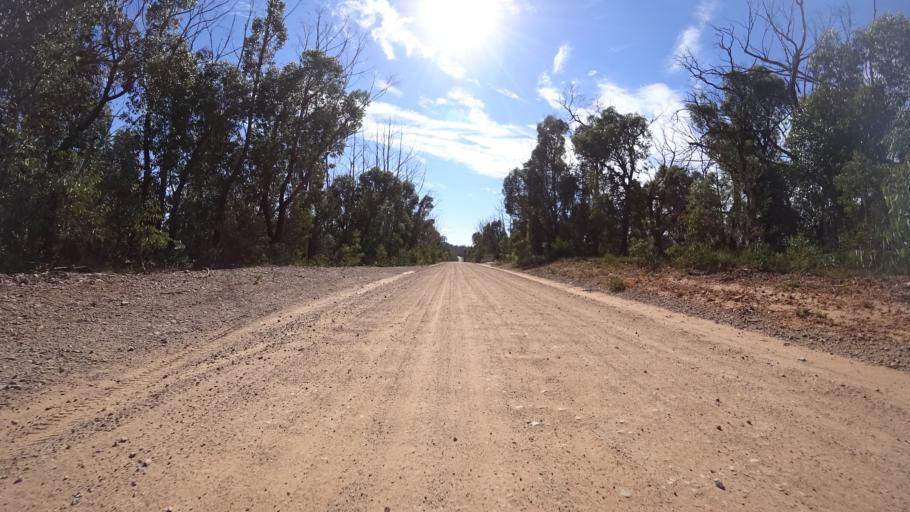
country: AU
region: New South Wales
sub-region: Lithgow
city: Lithgow
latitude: -33.4340
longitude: 150.1866
